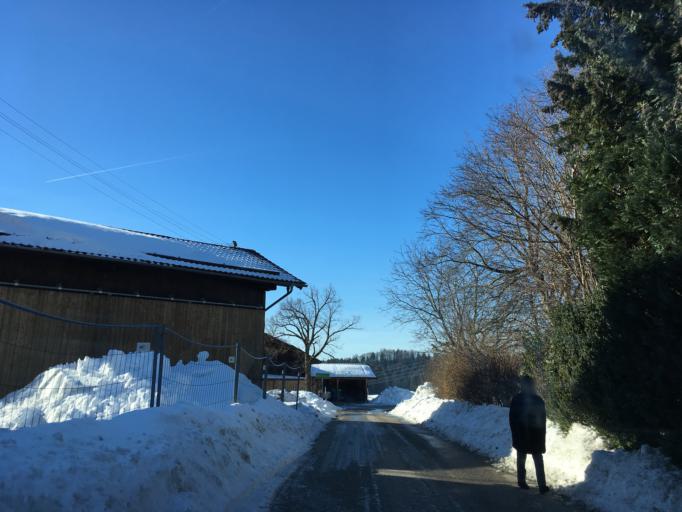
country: DE
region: Bavaria
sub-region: Upper Bavaria
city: Aschau im Chiemgau
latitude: 47.8144
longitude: 12.3346
